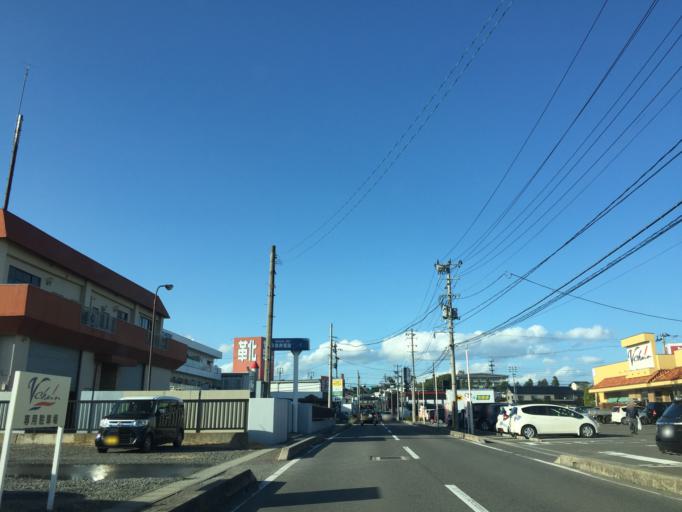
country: JP
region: Fukushima
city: Koriyama
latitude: 37.4172
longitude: 140.3590
